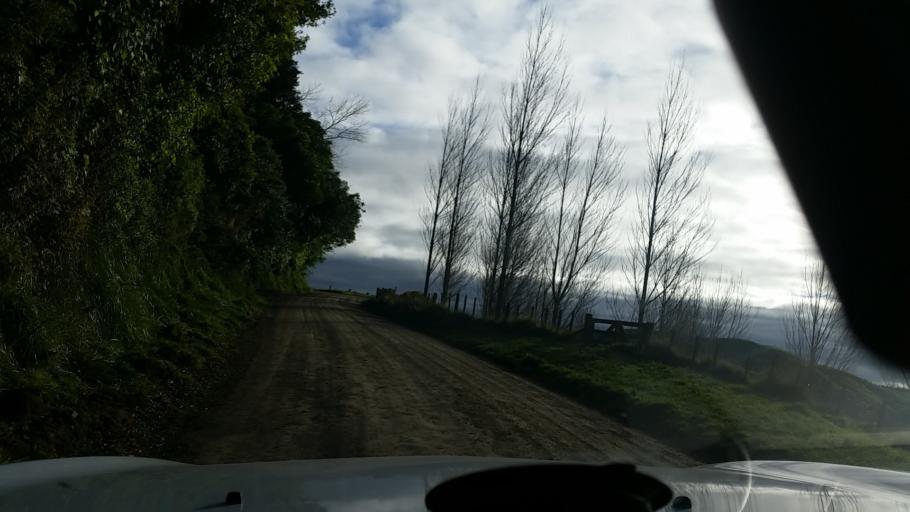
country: NZ
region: Hawke's Bay
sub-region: Napier City
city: Napier
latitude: -39.2624
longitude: 176.8518
